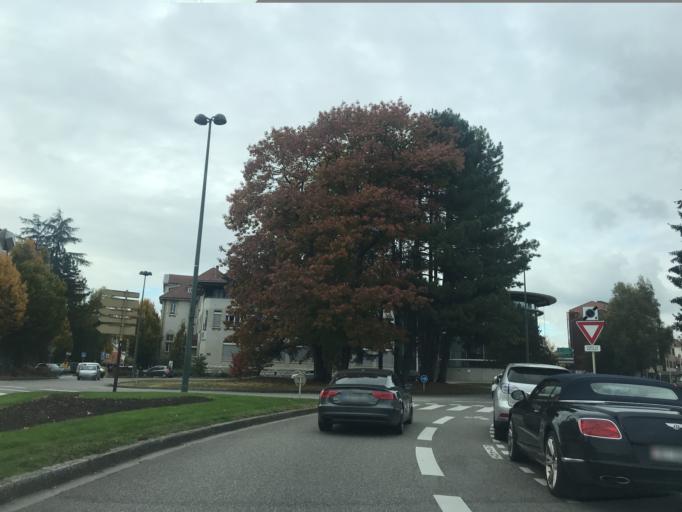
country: FR
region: Rhone-Alpes
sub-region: Departement de la Haute-Savoie
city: Annecy
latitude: 45.9058
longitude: 6.1314
